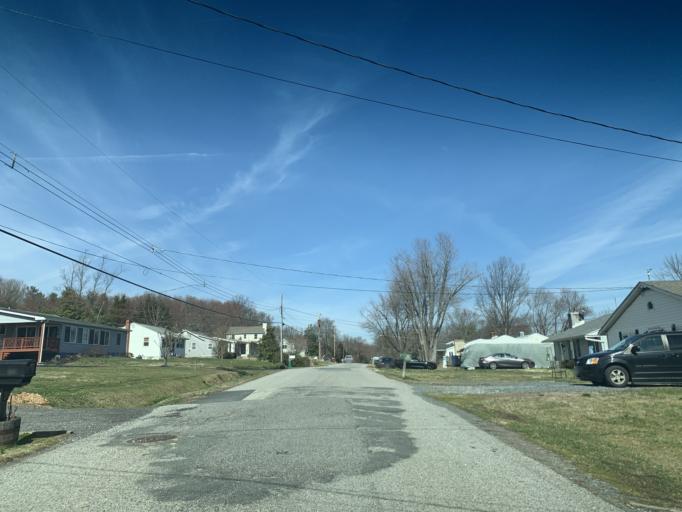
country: US
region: Maryland
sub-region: Cecil County
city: Charlestown
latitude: 39.5427
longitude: -76.0059
